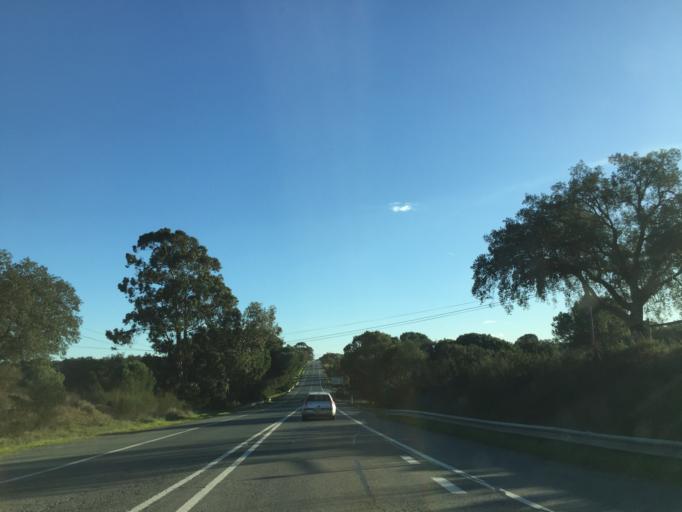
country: PT
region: Setubal
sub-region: Grandola
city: Grandola
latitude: 38.1085
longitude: -8.4183
